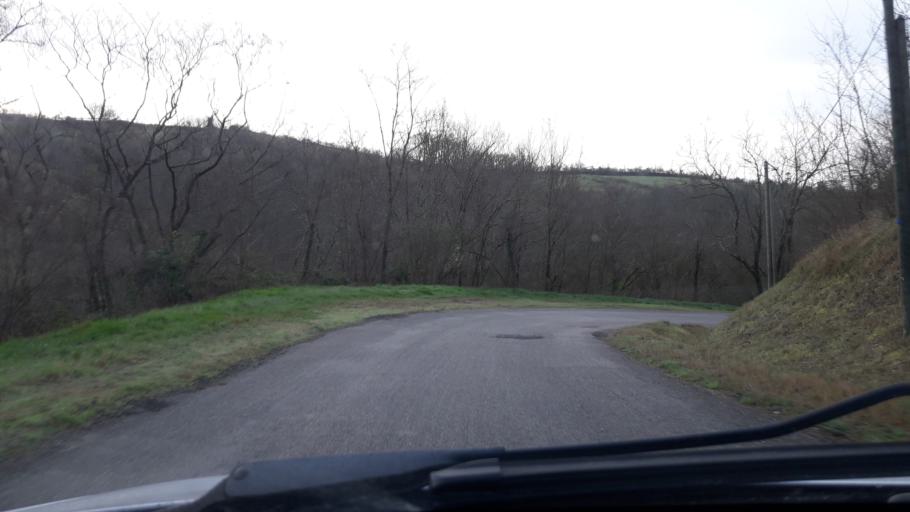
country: FR
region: Midi-Pyrenees
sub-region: Departement de la Haute-Garonne
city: Montesquieu-Volvestre
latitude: 43.1748
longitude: 1.2839
